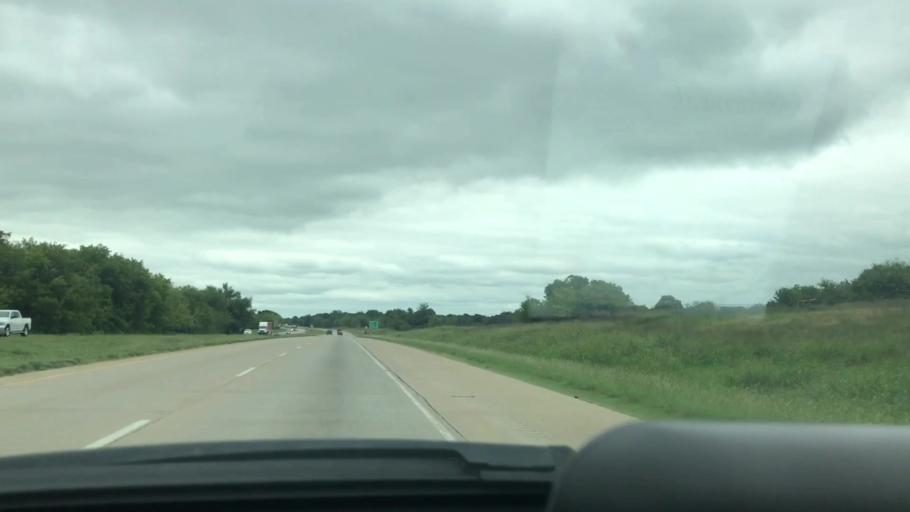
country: US
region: Oklahoma
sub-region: Mayes County
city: Chouteau
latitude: 36.1958
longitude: -95.3415
